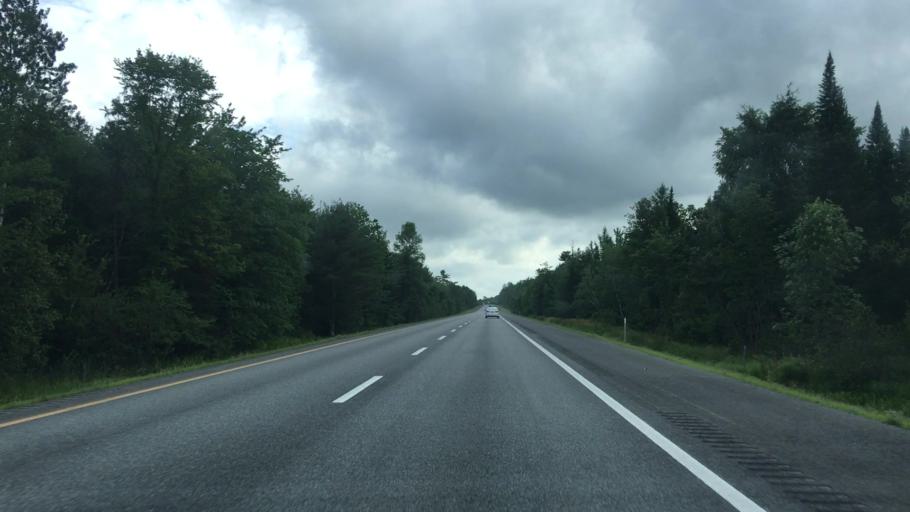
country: US
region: Maine
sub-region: Waldo County
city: Burnham
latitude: 44.7037
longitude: -69.4580
